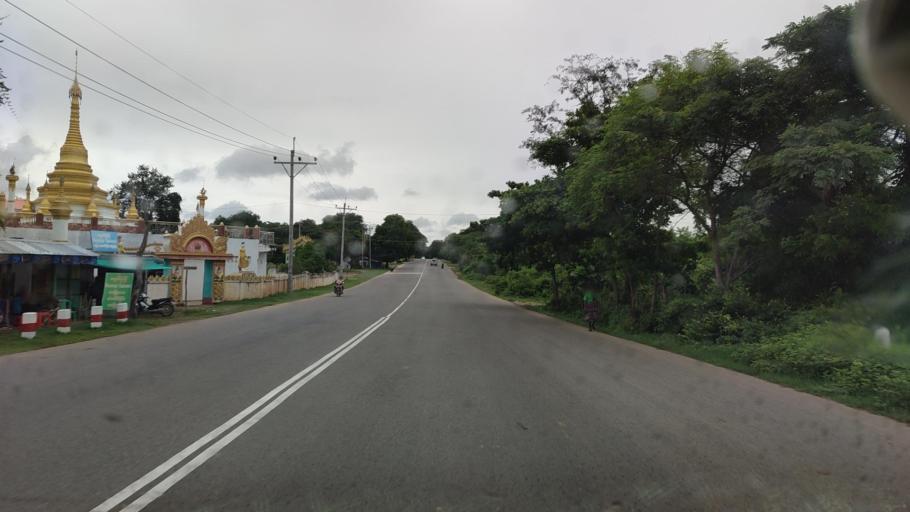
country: MM
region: Mandalay
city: Meiktila
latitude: 20.8144
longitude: 95.9074
